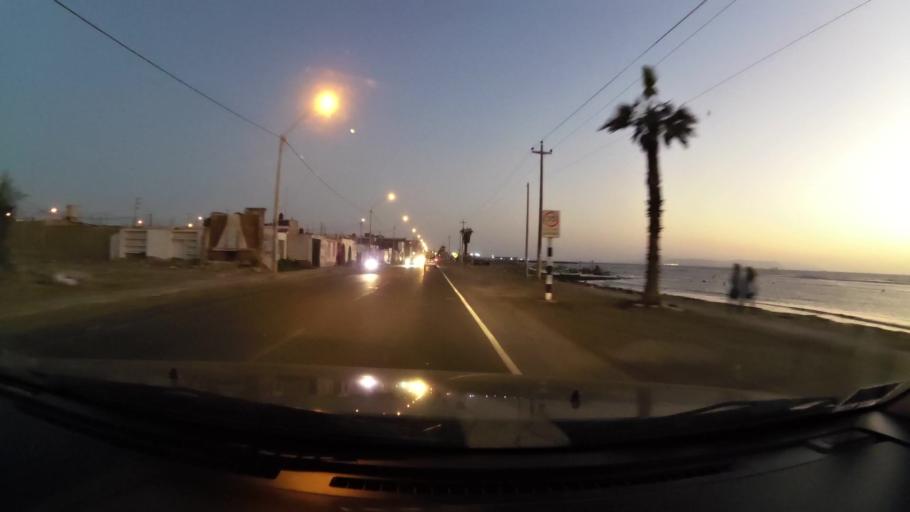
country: PE
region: Ica
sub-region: Provincia de Pisco
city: Pisco
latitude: -13.7280
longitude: -76.2227
